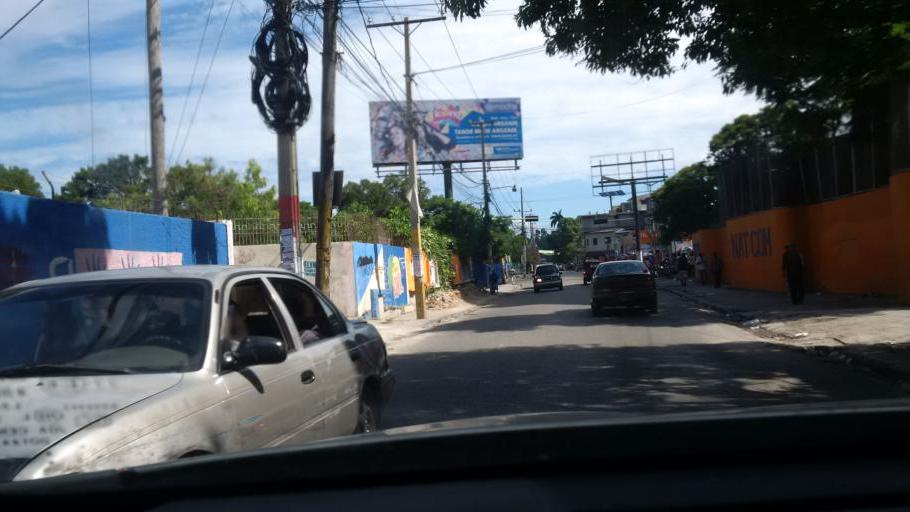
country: HT
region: Ouest
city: Port-au-Prince
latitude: 18.5358
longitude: -72.3237
